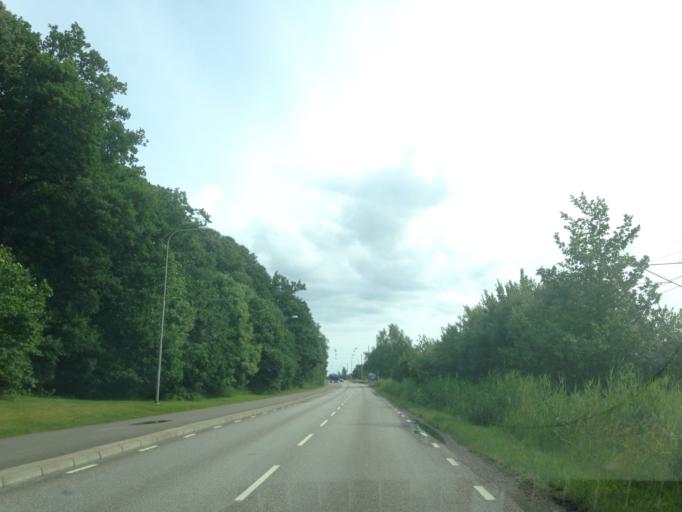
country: SE
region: Vaestra Goetaland
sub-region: Goteborg
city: Goeteborg
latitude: 57.7562
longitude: 11.9467
